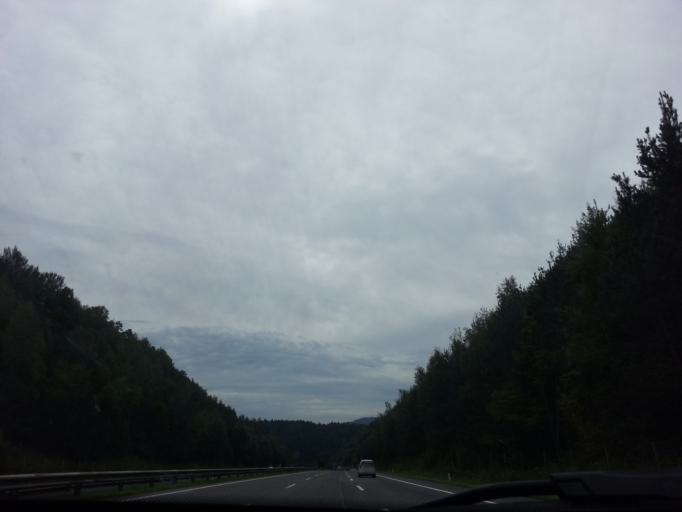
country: AT
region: Styria
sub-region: Politischer Bezirk Graz-Umgebung
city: Gratkorn
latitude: 47.1355
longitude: 15.3558
